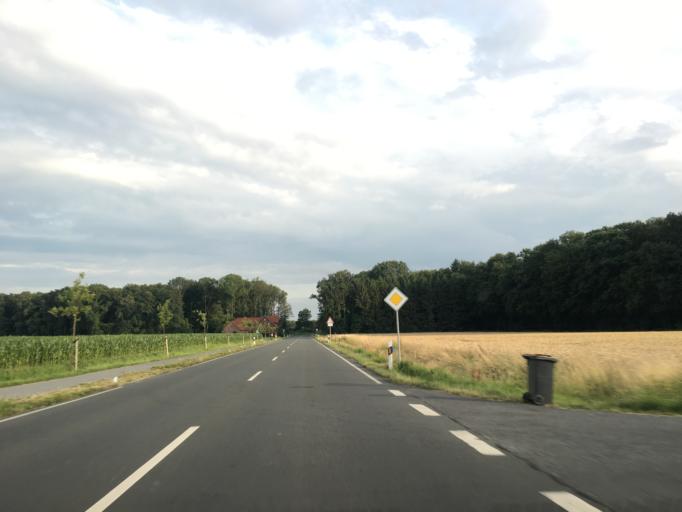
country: DE
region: North Rhine-Westphalia
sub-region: Regierungsbezirk Munster
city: Senden
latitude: 51.9336
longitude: 7.5279
